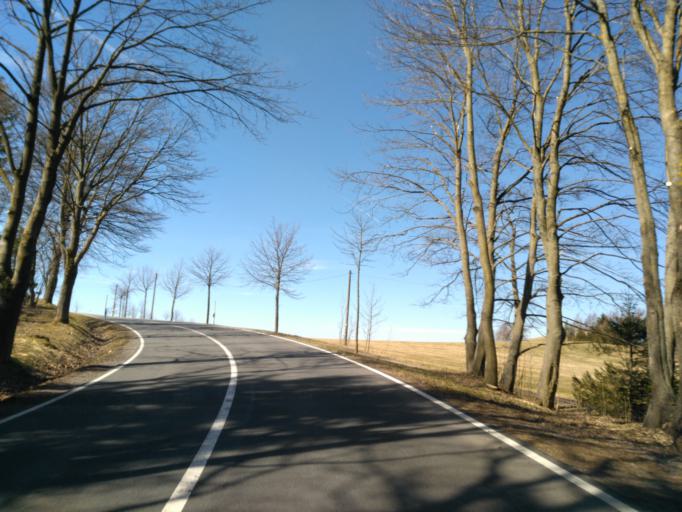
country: DE
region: Saxony
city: Rittersgrun
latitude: 50.4771
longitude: 12.7802
